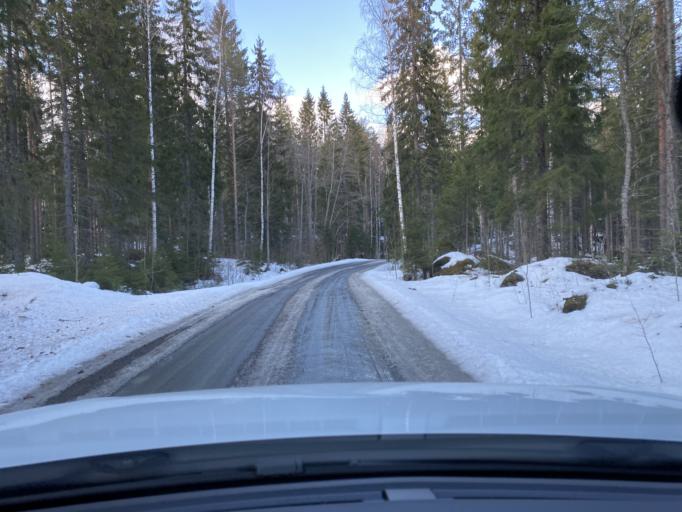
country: FI
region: Pirkanmaa
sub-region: Lounais-Pirkanmaa
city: Mouhijaervi
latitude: 61.4515
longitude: 22.9209
